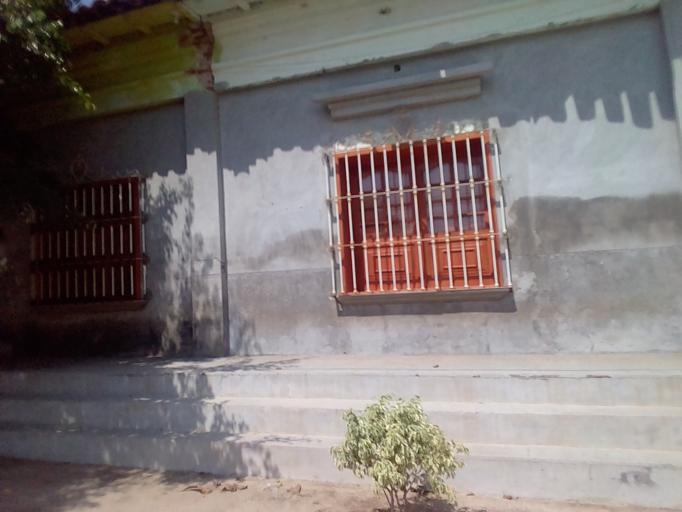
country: MX
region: Oaxaca
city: Union Hidalgo
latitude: 16.4714
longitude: -94.8292
